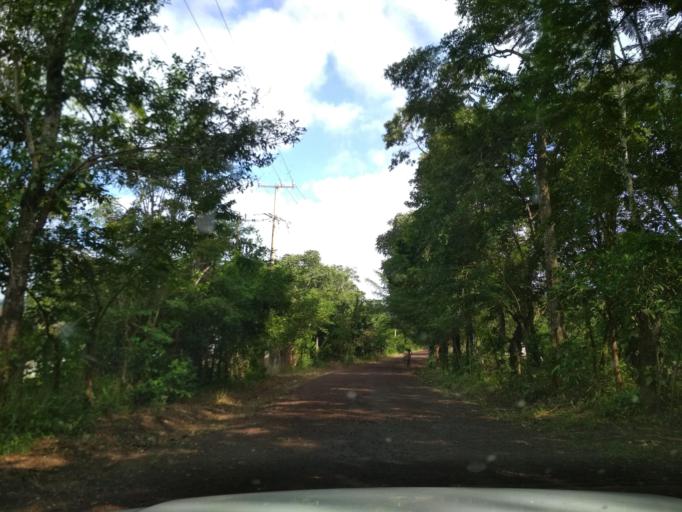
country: MX
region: Veracruz
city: Catemaco
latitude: 18.3712
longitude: -95.1132
